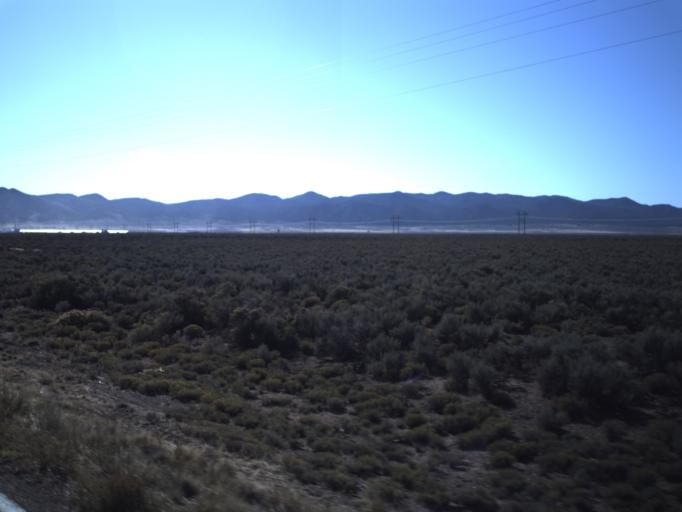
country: US
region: Utah
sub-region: Washington County
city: Enterprise
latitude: 37.6951
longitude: -113.6162
